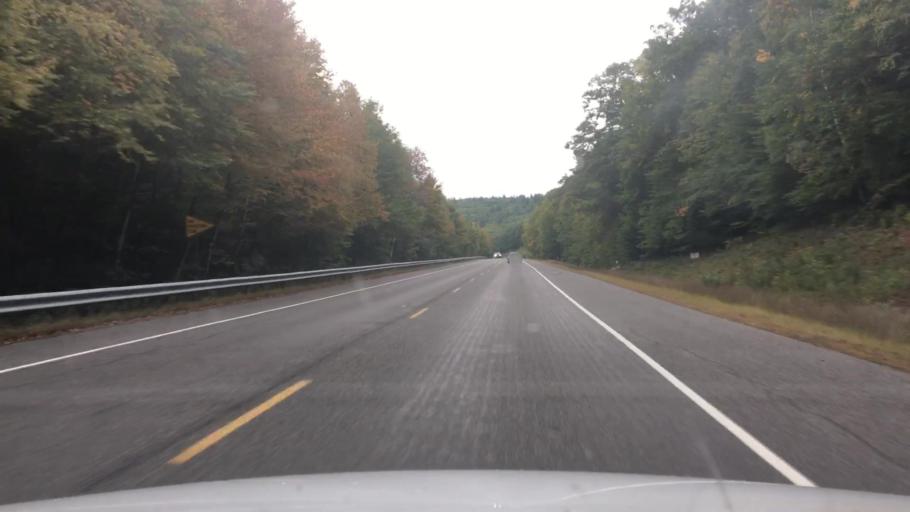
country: US
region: New Hampshire
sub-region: Carroll County
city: Wolfeboro
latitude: 43.5250
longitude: -71.2740
